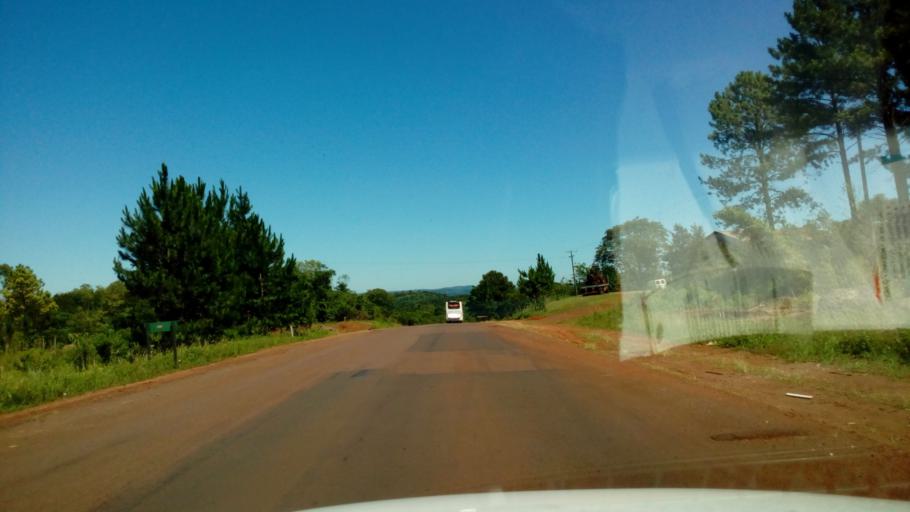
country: AR
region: Misiones
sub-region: Departamento de Leandro N. Alem
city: Leandro N. Alem
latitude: -27.5971
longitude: -55.3510
